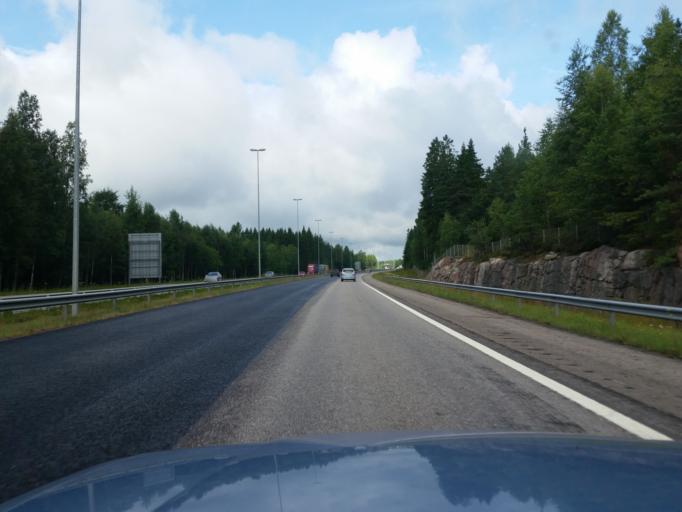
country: FI
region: Uusimaa
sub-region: Helsinki
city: Espoo
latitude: 60.2478
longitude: 24.5461
